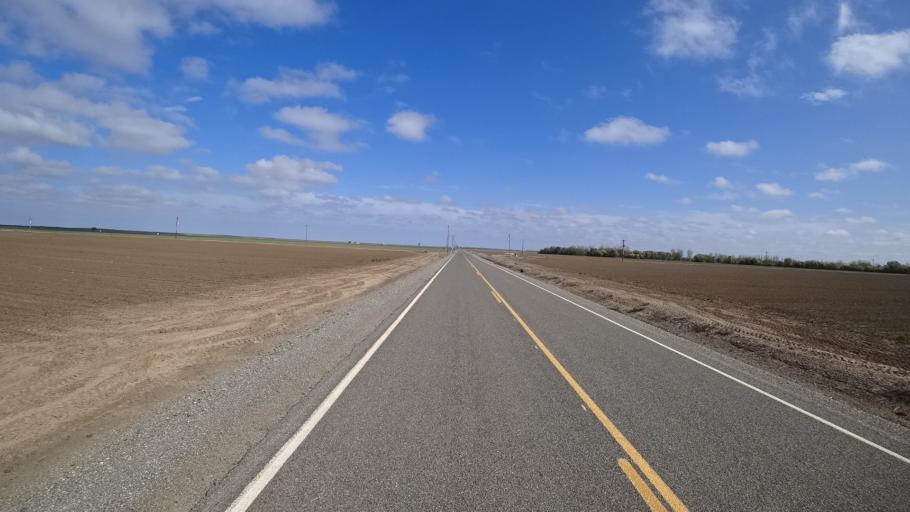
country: US
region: California
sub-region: Butte County
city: Biggs
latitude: 39.4187
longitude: -121.9295
